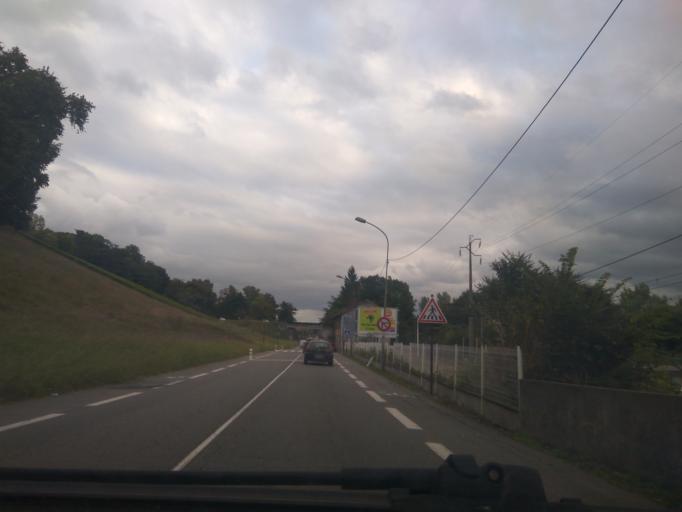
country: FR
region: Aquitaine
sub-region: Departement des Pyrenees-Atlantiques
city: Bizanos
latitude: 43.2863
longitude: -0.3494
